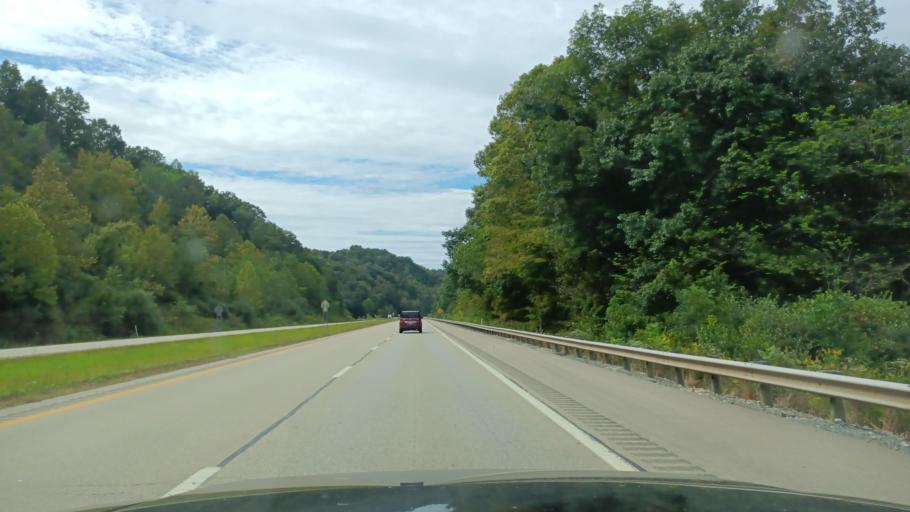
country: US
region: West Virginia
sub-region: Doddridge County
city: West Union
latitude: 39.2779
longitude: -80.7900
